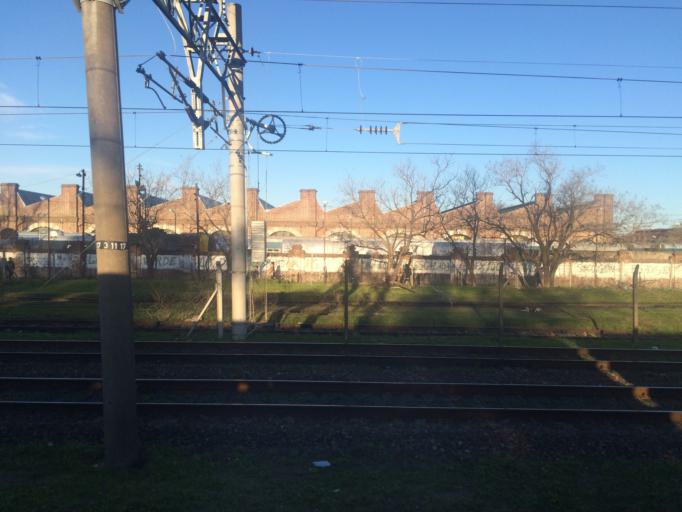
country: AR
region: Buenos Aires
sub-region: Partido de Lanus
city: Lanus
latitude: -34.7292
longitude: -58.3939
